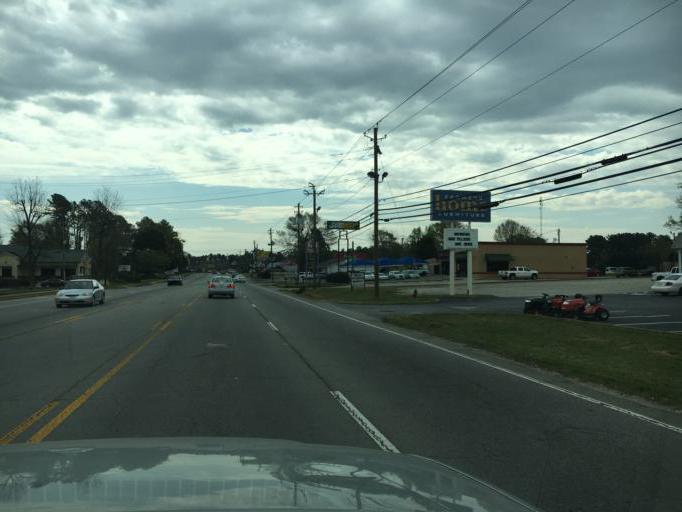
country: US
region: Georgia
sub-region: Stephens County
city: Toccoa
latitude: 34.5691
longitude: -83.3046
